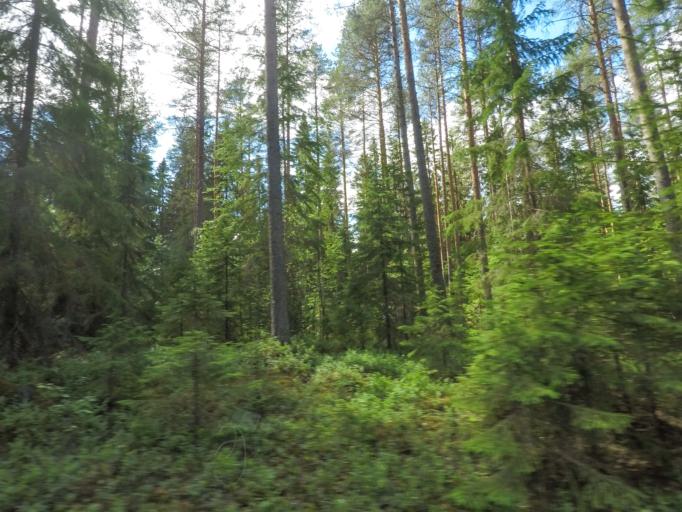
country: FI
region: Central Finland
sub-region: Jyvaeskylae
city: Hankasalmi
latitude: 62.4126
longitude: 26.6436
